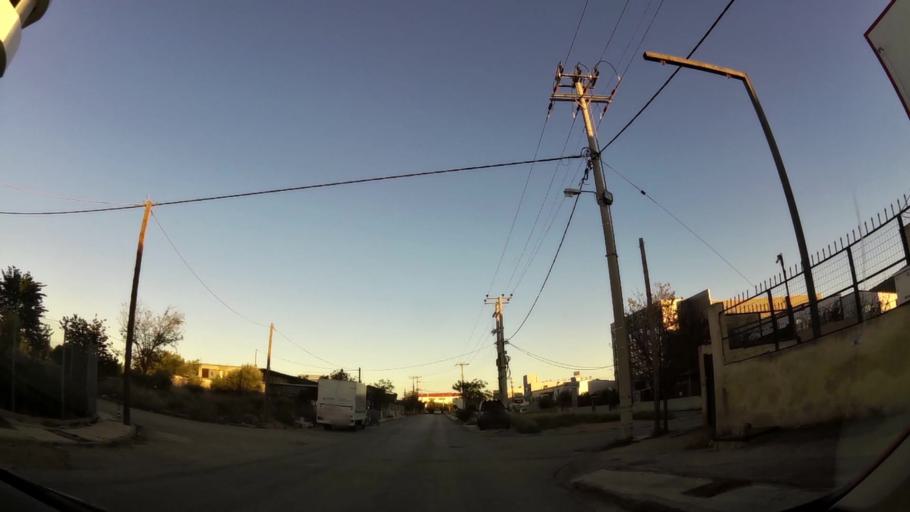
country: GR
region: Attica
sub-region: Nomarchia Dytikis Attikis
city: Ano Liosia
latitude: 38.0763
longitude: 23.6870
